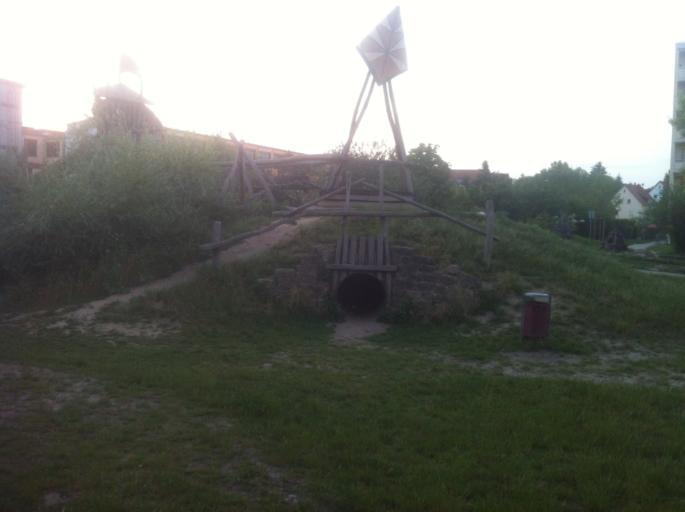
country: DE
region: Saxony
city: Coswig
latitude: 51.1275
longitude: 13.5891
